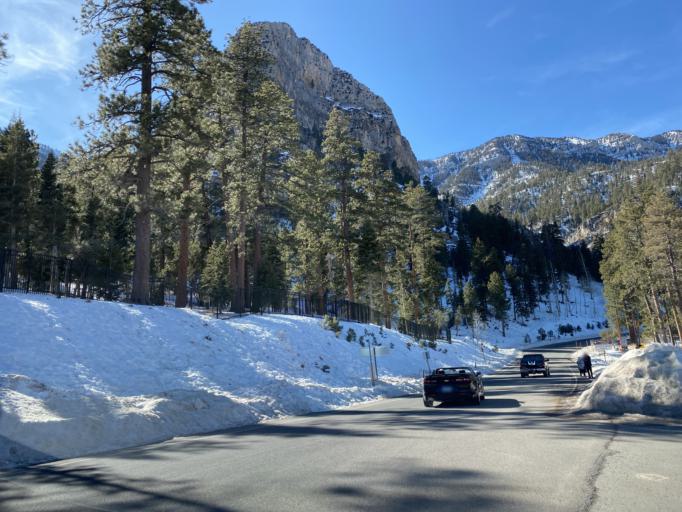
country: US
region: Nevada
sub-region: Nye County
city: Pahrump
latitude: 36.2574
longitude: -115.6461
